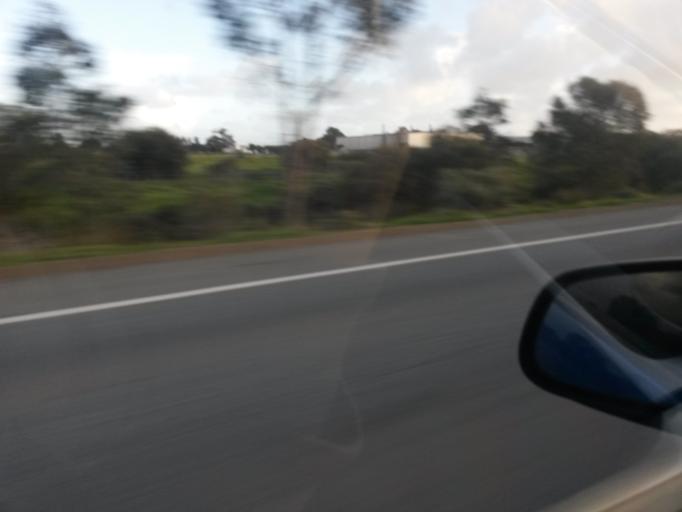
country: AU
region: South Australia
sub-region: Port Adelaide Enfield
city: Alberton
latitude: -34.8343
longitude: 138.5355
